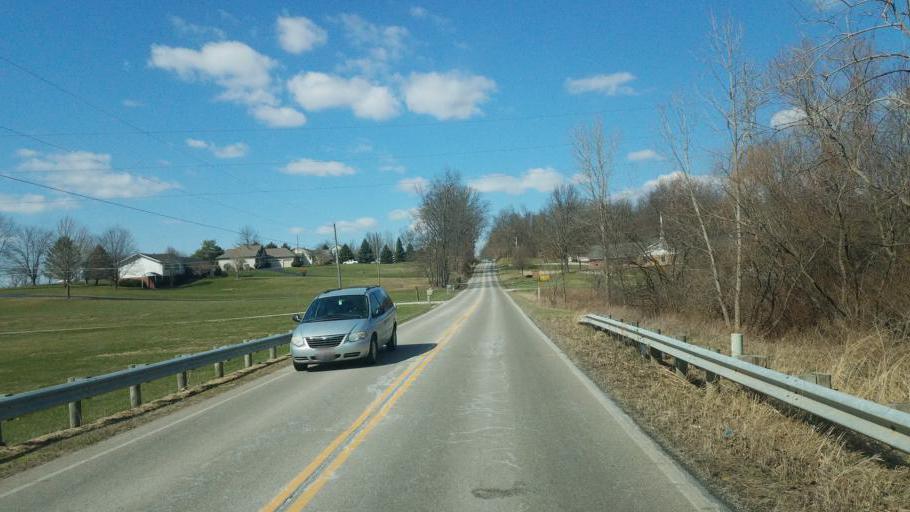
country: US
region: Ohio
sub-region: Knox County
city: Mount Vernon
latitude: 40.4172
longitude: -82.4953
